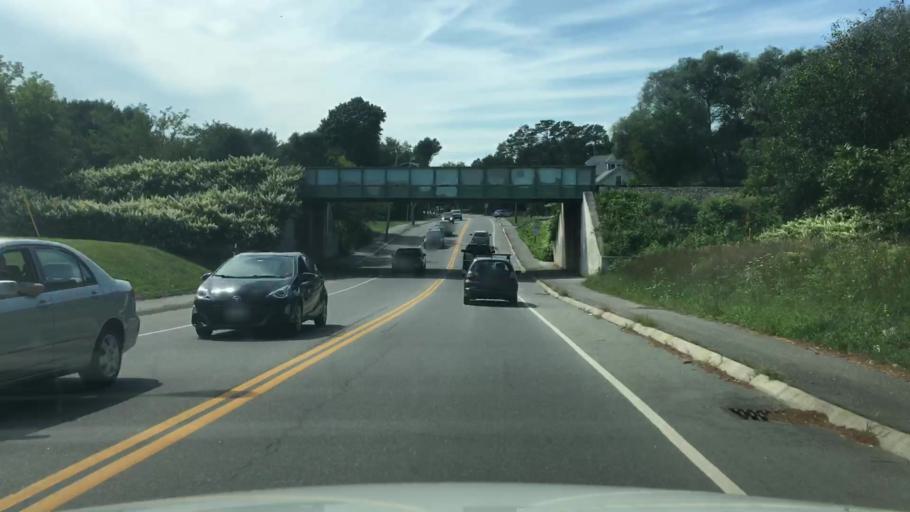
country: US
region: Maine
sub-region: Cumberland County
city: South Portland Gardens
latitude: 43.6297
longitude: -70.2952
